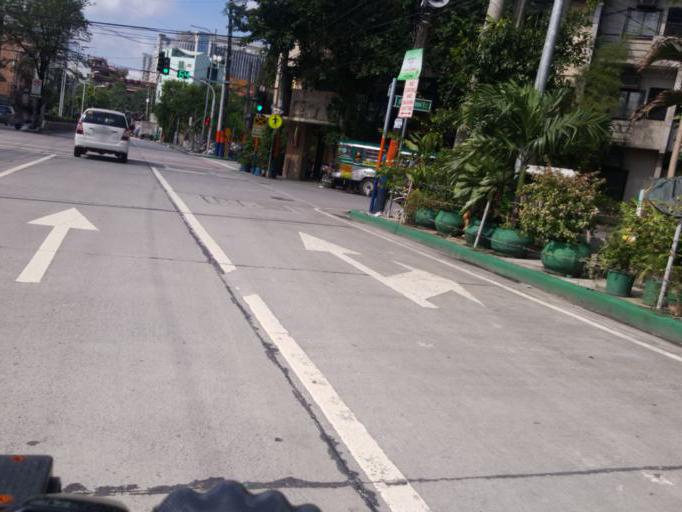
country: PH
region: Metro Manila
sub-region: City of Manila
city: Manila
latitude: 14.6136
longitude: 120.9865
